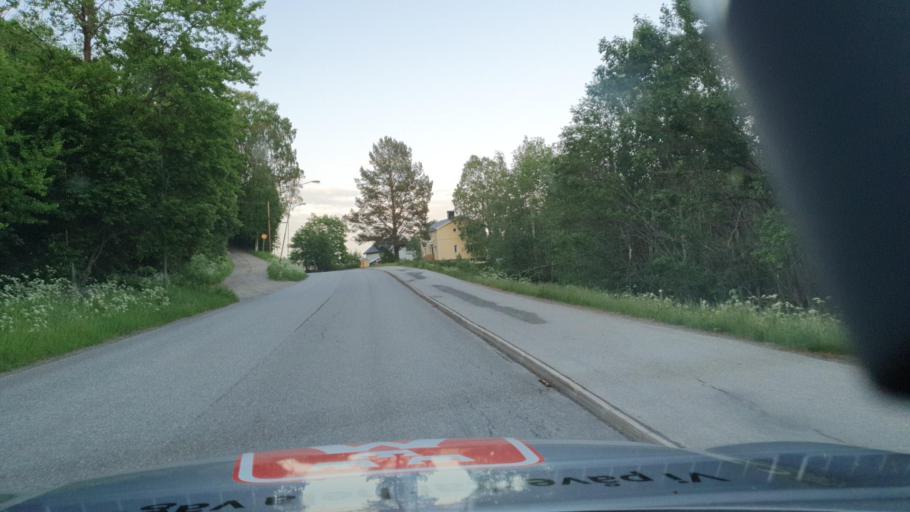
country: SE
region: Vaesternorrland
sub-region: OErnskoeldsviks Kommun
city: Bjasta
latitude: 63.2860
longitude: 18.5468
